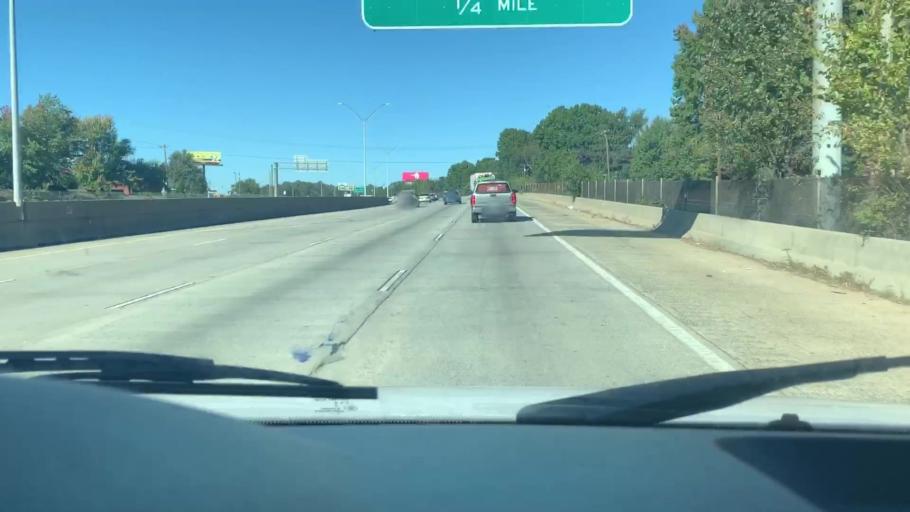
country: US
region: North Carolina
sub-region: Mecklenburg County
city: Charlotte
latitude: 35.2413
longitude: -80.9296
